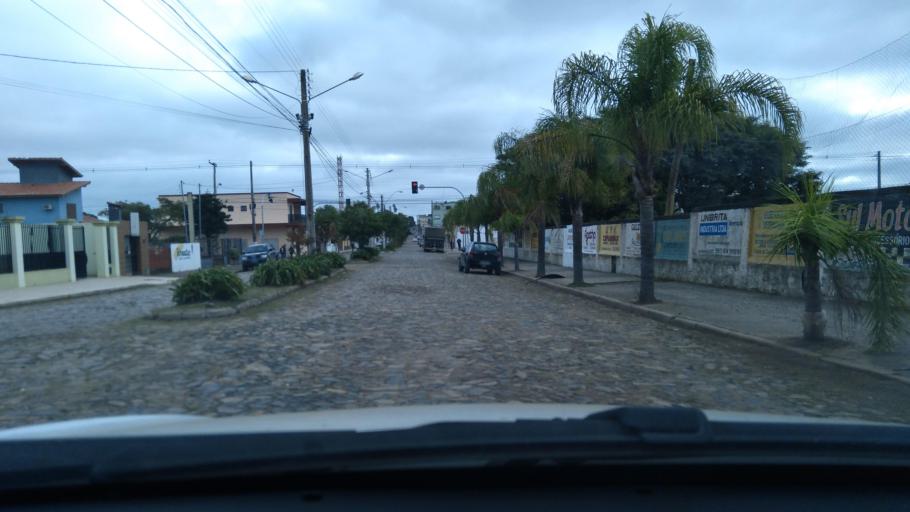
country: BR
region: Rio Grande do Sul
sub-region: Dom Pedrito
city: Dom Pedrito
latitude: -30.9861
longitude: -54.6667
